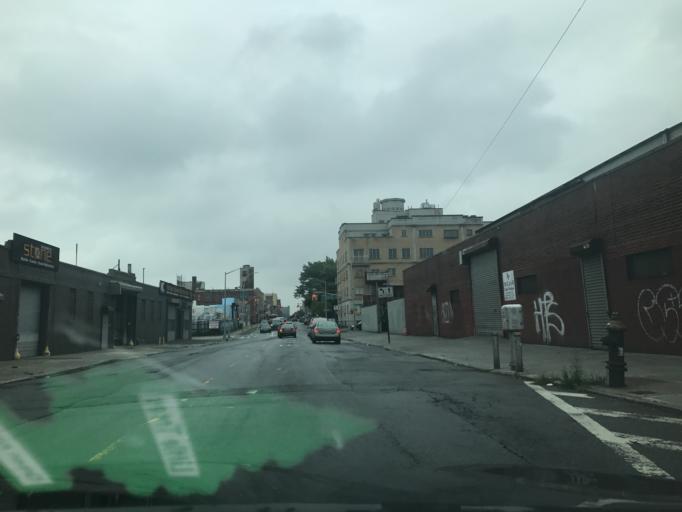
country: US
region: New York
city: New York City
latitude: 40.6961
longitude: -73.9624
